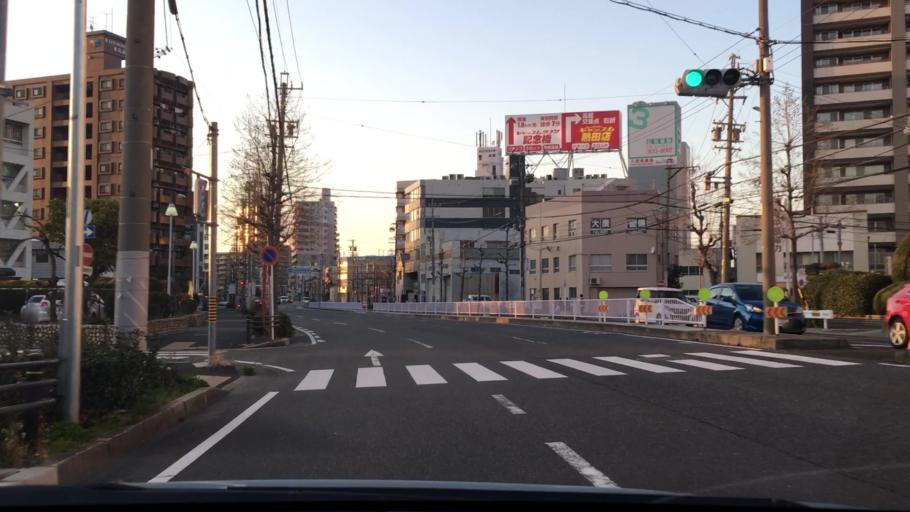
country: JP
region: Aichi
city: Nagoya-shi
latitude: 35.1326
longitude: 136.9081
